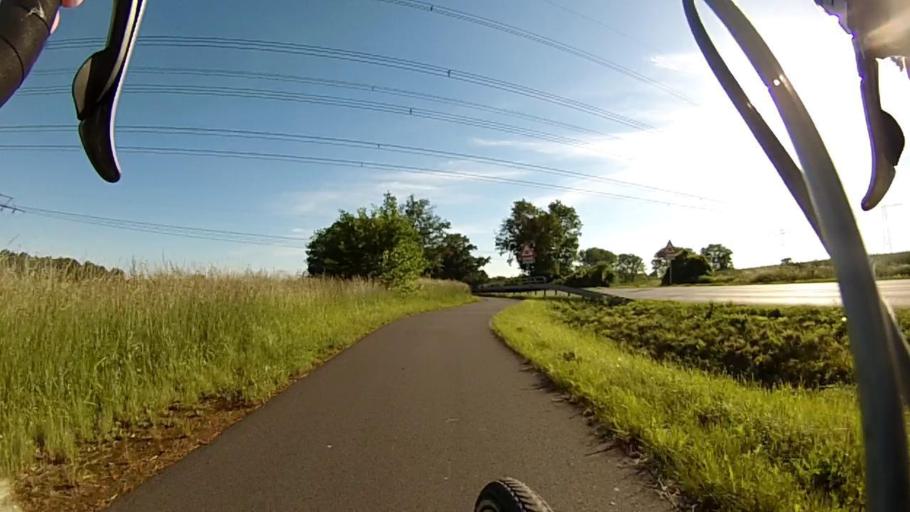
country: DE
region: Brandenburg
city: Werneuchen
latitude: 52.6140
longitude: 13.6552
